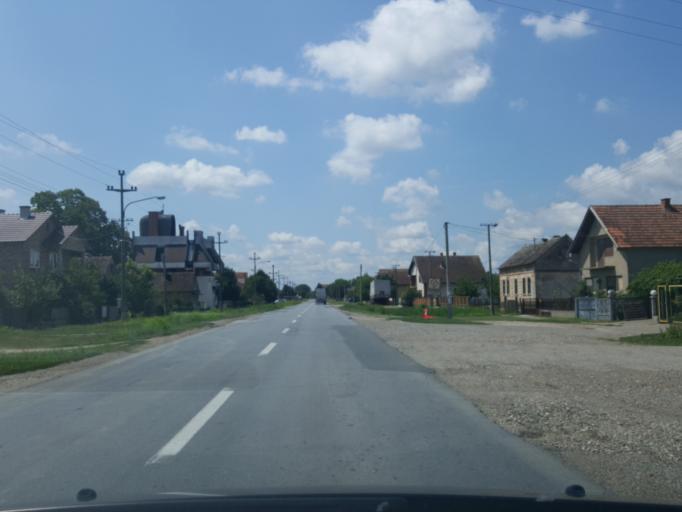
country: RS
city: Salas Nocajski
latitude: 44.9460
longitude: 19.5842
